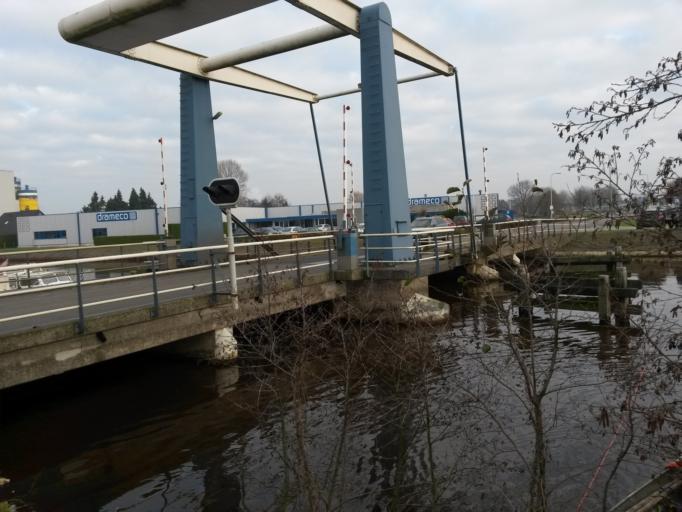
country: NL
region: Drenthe
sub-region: Gemeente Coevorden
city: Coevorden
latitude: 52.6561
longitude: 6.7315
